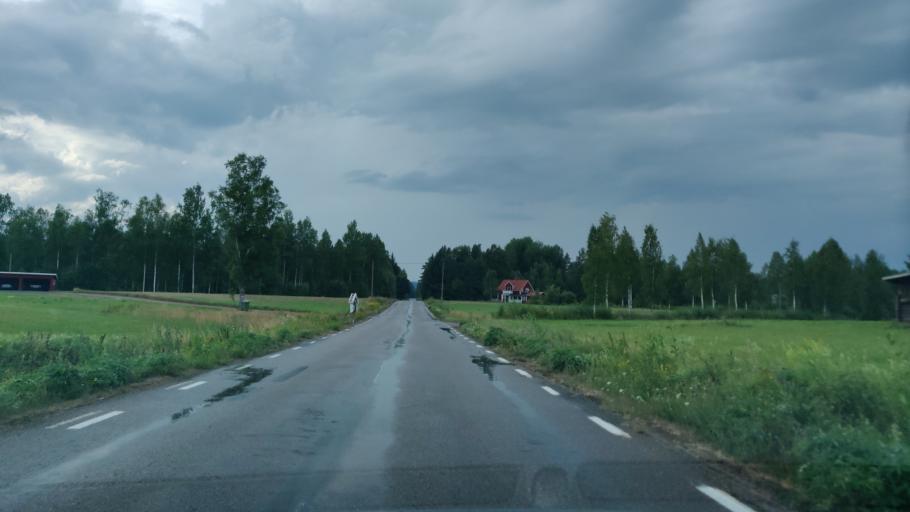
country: SE
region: Vaermland
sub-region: Munkfors Kommun
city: Munkfors
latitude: 59.8698
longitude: 13.5358
